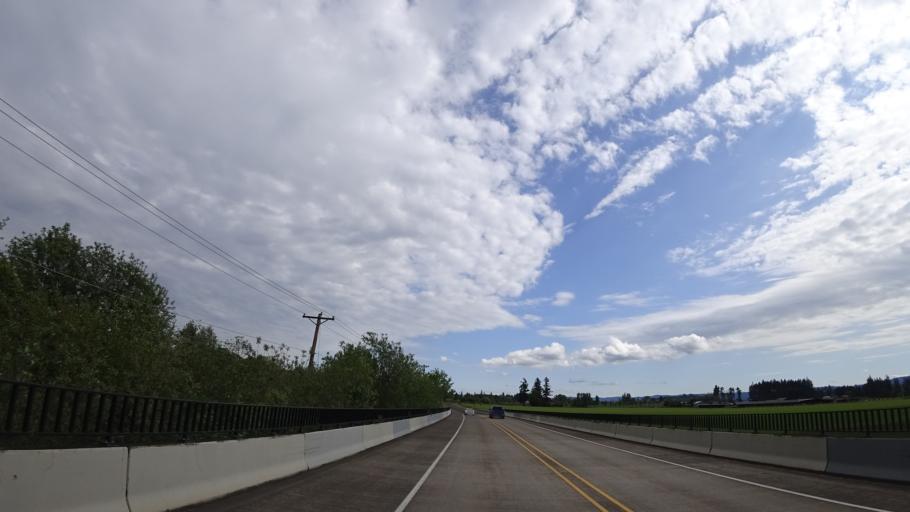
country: US
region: Oregon
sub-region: Washington County
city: Hillsboro
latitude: 45.4894
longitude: -122.9514
